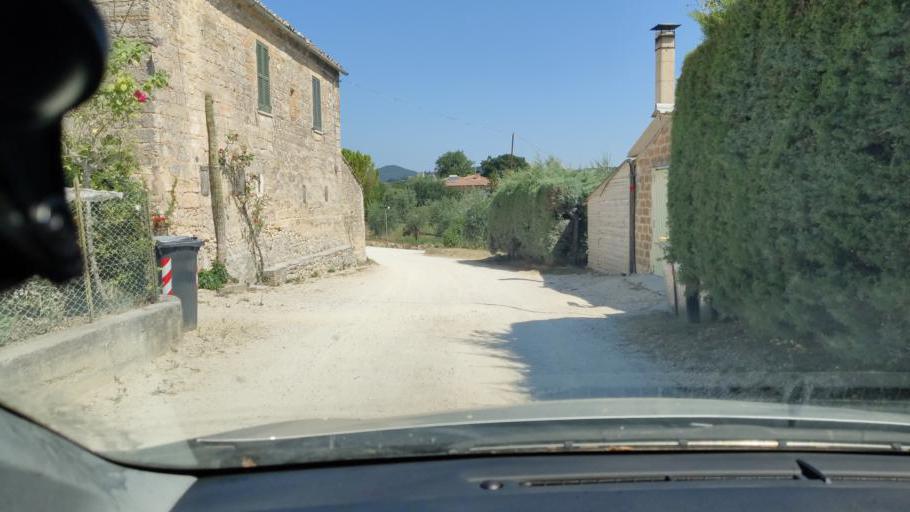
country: IT
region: Umbria
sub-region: Provincia di Terni
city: Fornole
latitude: 42.5441
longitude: 12.4416
